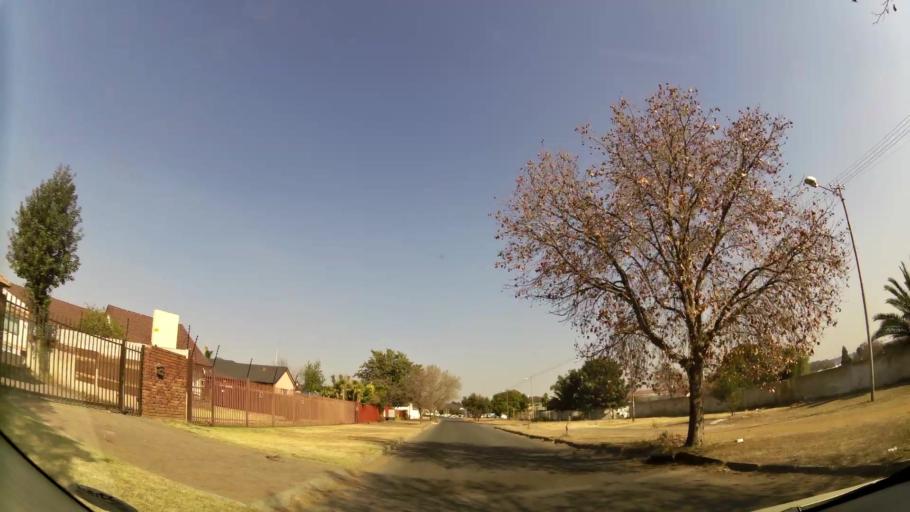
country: ZA
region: Gauteng
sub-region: West Rand District Municipality
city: Randfontein
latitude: -26.1641
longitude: 27.6988
